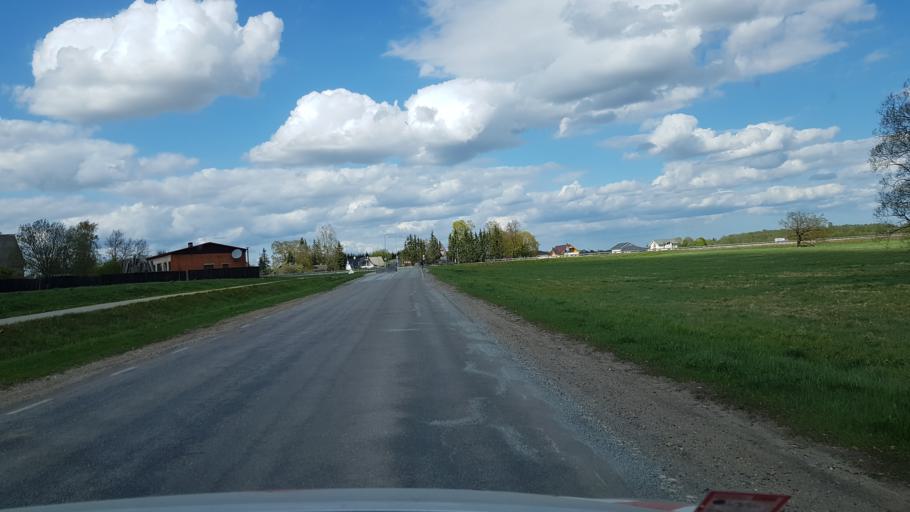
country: EE
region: Tartu
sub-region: Tartu linn
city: Tartu
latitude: 58.3702
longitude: 26.7988
